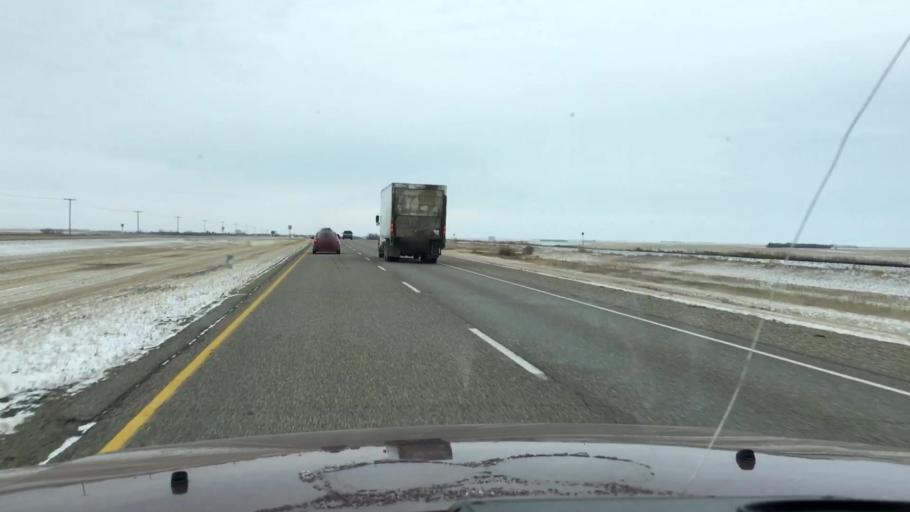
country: CA
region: Saskatchewan
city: Watrous
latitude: 51.1811
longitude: -105.9399
